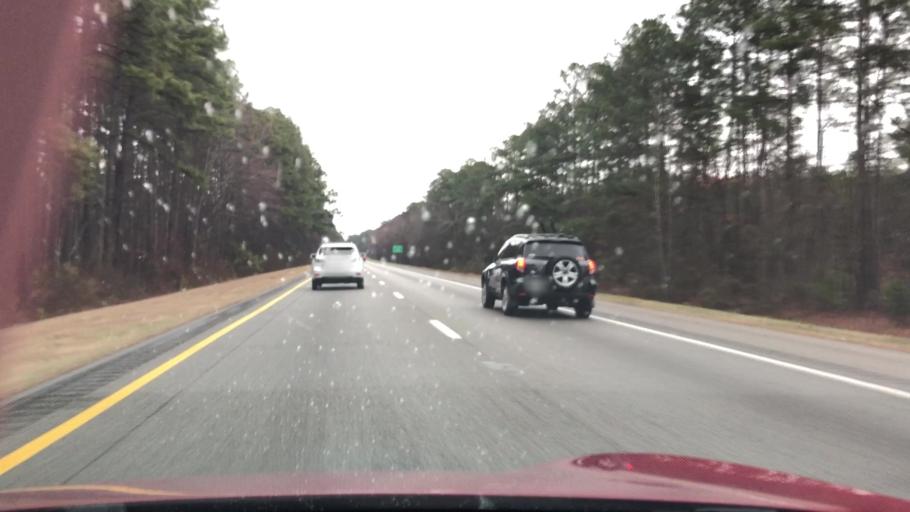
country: US
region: South Carolina
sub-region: Dillon County
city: Latta
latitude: 34.3358
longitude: -79.5517
